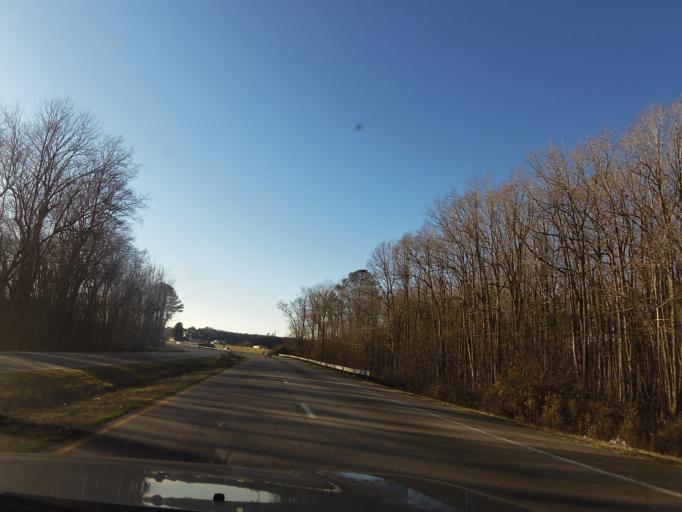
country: US
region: Virginia
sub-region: Isle of Wight County
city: Windsor
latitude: 36.6951
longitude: -76.7252
